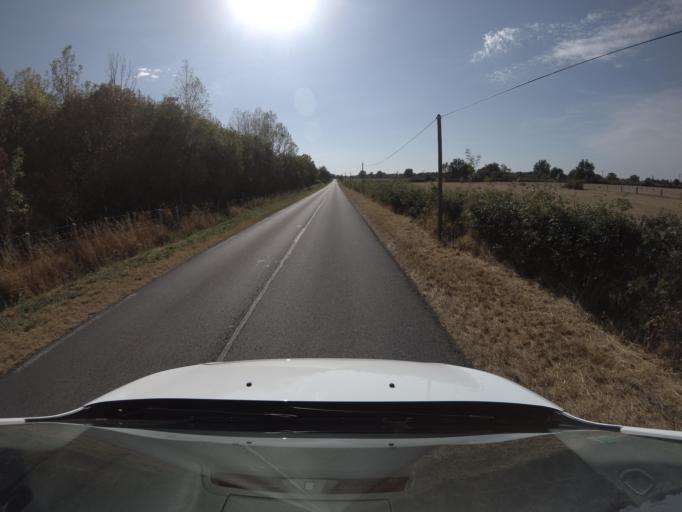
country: FR
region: Poitou-Charentes
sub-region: Departement des Deux-Sevres
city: Argenton-les-Vallees
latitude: 47.0007
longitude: -0.3903
